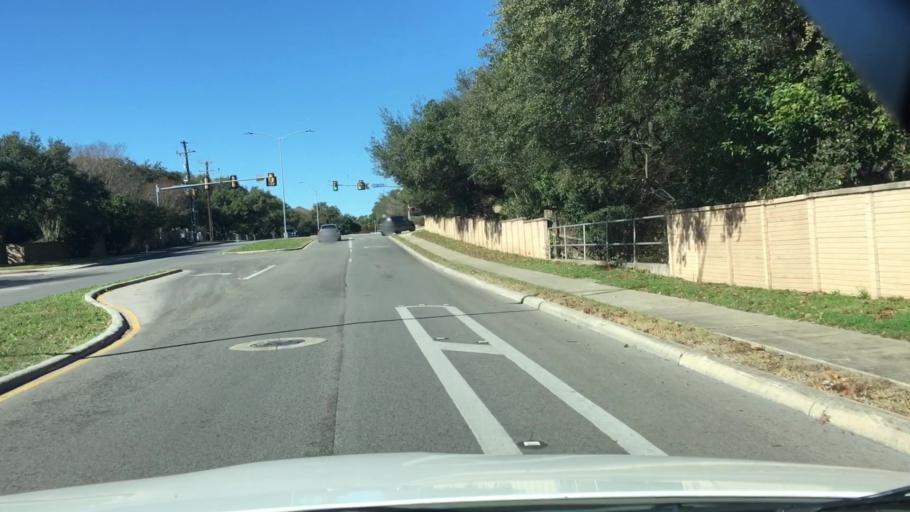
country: US
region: Texas
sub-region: Bexar County
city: Hollywood Park
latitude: 29.6021
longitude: -98.4583
